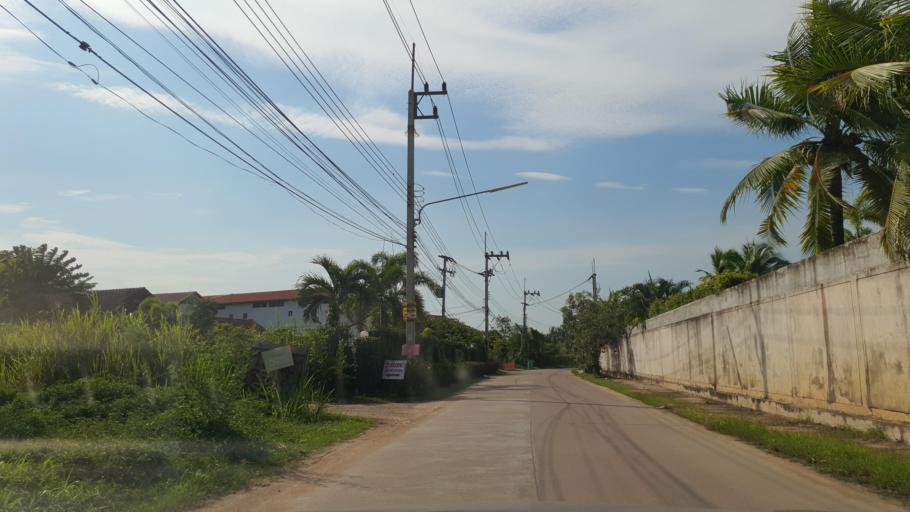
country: TH
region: Chon Buri
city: Phatthaya
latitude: 12.8033
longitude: 100.9326
